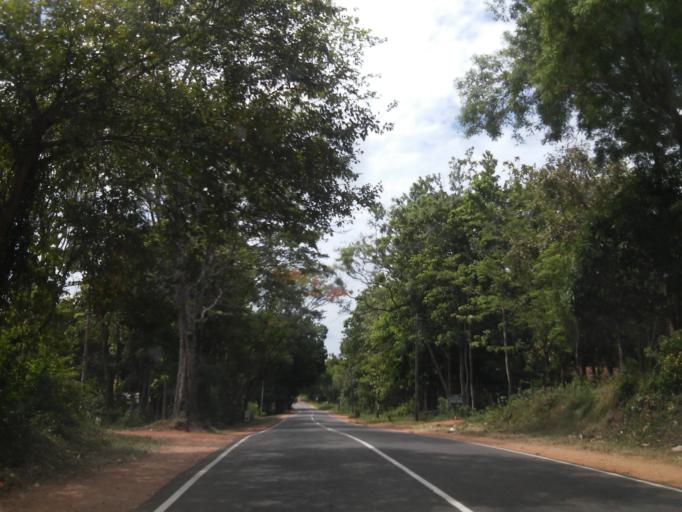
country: LK
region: Central
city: Sigiriya
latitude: 8.0726
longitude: 80.6868
